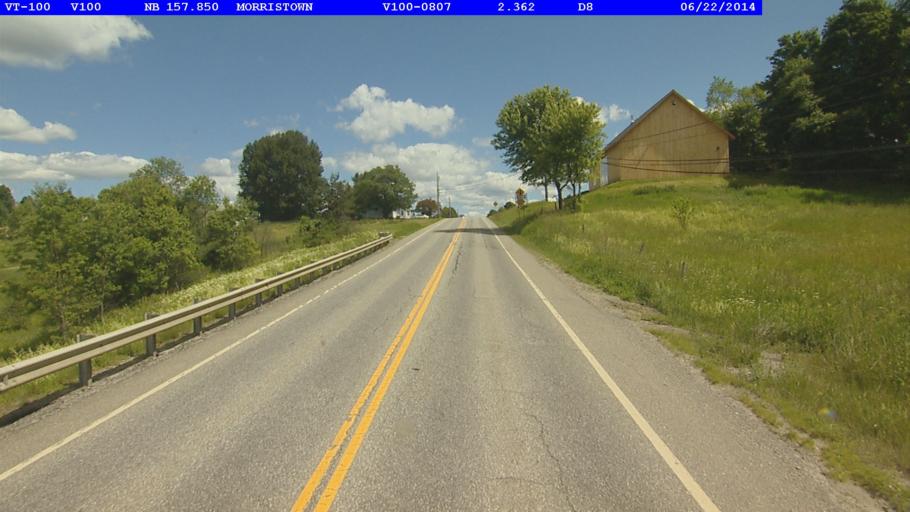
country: US
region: Vermont
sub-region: Lamoille County
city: Morristown
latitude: 44.5263
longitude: -72.6182
